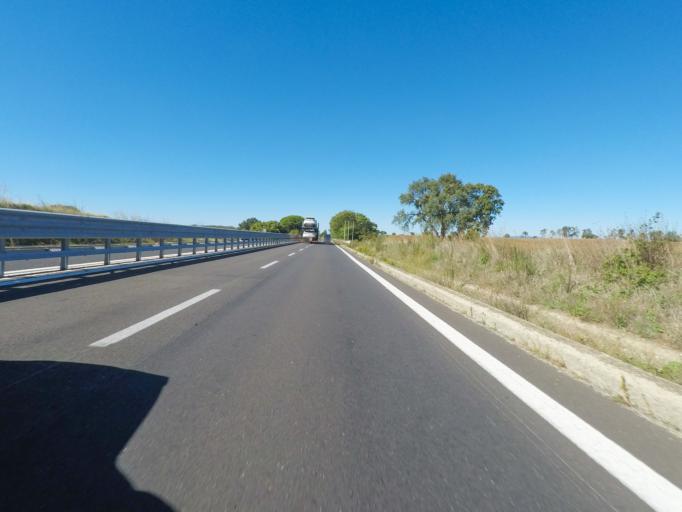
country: IT
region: Latium
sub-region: Provincia di Viterbo
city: Montalto di Castro
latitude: 42.3028
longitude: 11.6671
